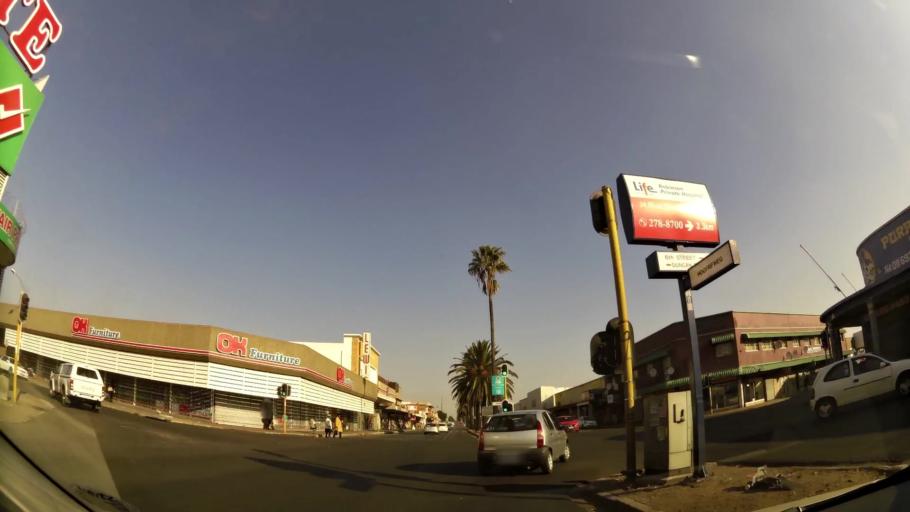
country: ZA
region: Gauteng
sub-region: West Rand District Municipality
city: Randfontein
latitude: -26.1791
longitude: 27.7043
